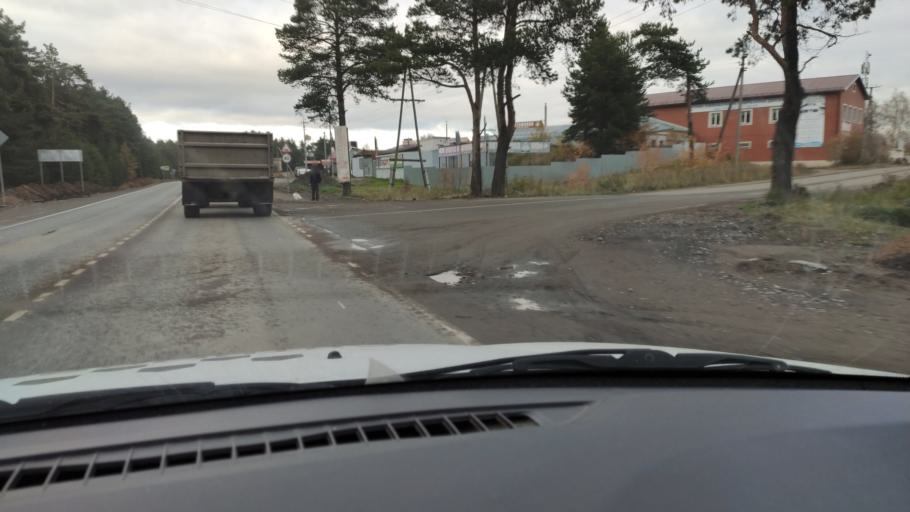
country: RU
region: Kirov
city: Belaya Kholunitsa
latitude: 58.8486
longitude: 50.8268
